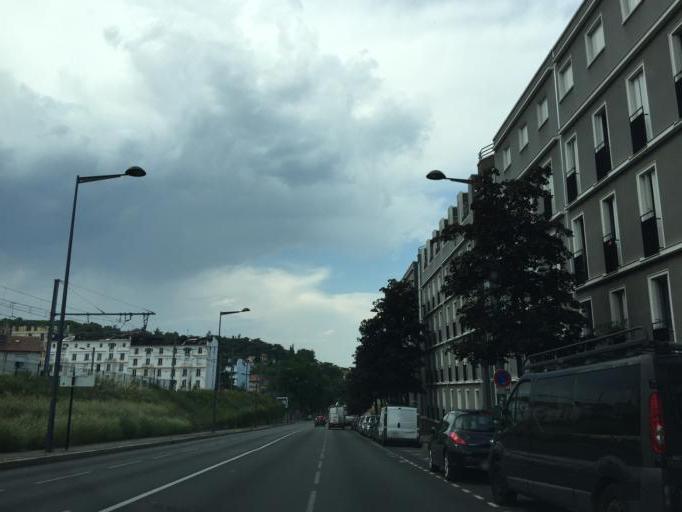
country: FR
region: Rhone-Alpes
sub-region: Departement de la Loire
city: Saint-Etienne
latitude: 45.4402
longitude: 4.3786
